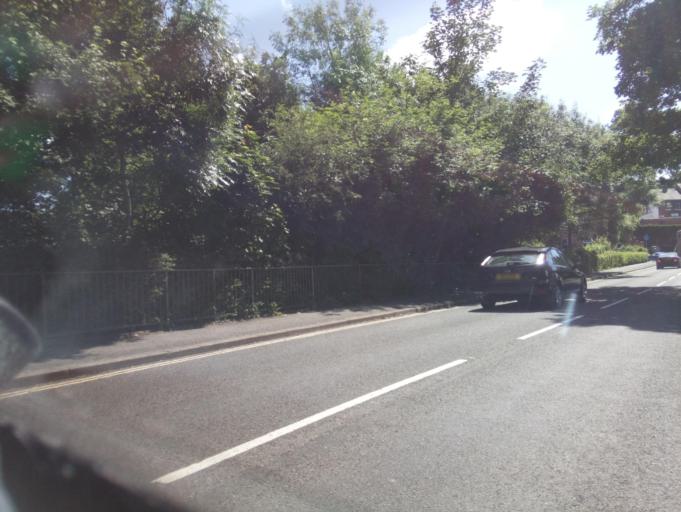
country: GB
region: England
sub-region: Derbyshire
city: Ashbourne
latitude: 53.0145
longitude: -1.7355
